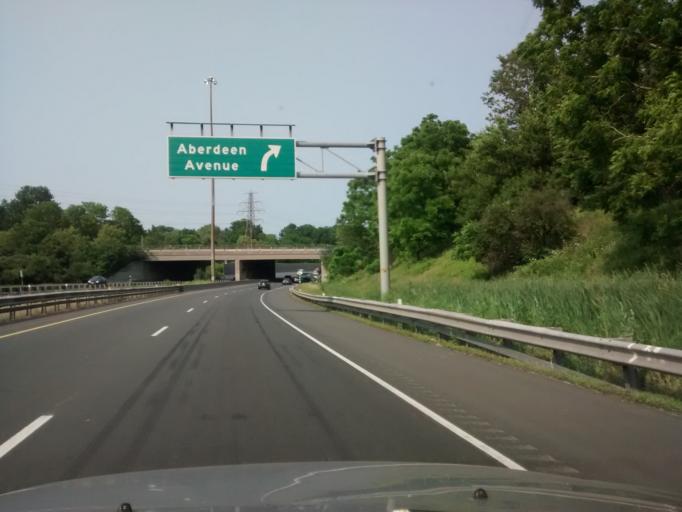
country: CA
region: Ontario
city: Hamilton
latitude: 43.2516
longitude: -79.9155
